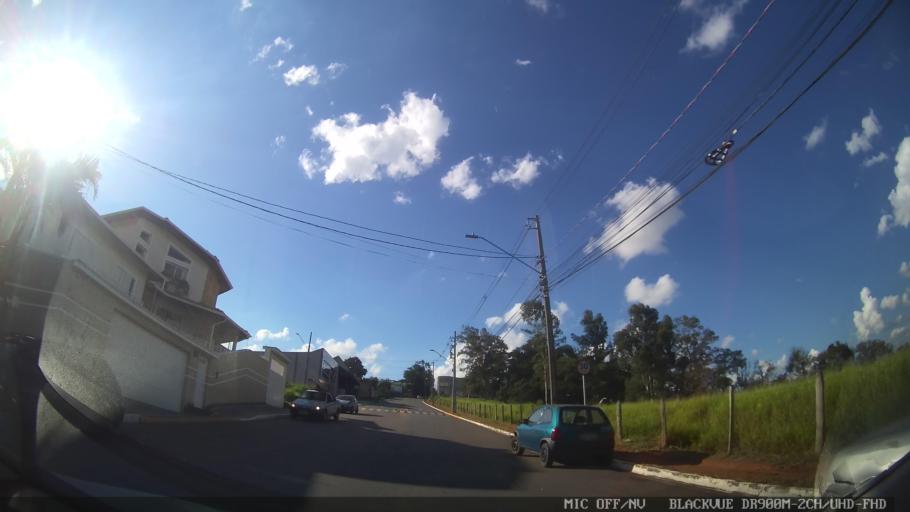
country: BR
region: Minas Gerais
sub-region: Extrema
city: Extrema
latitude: -22.8542
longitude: -46.3287
